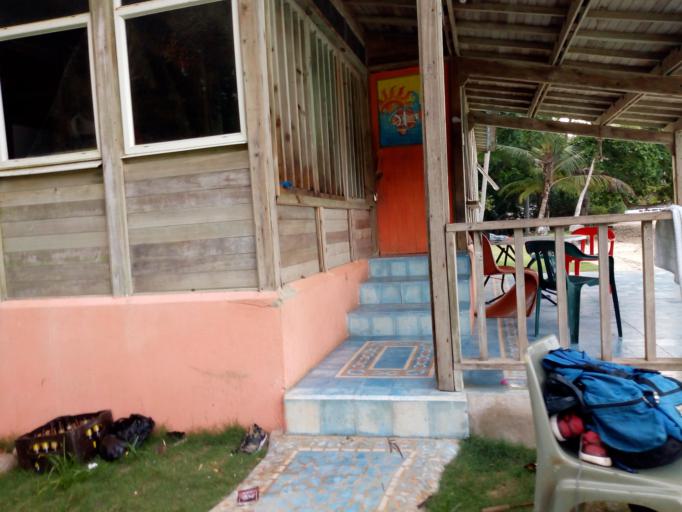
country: PA
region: Guna Yala
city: Puerto Obaldia
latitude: 8.6553
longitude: -77.3653
